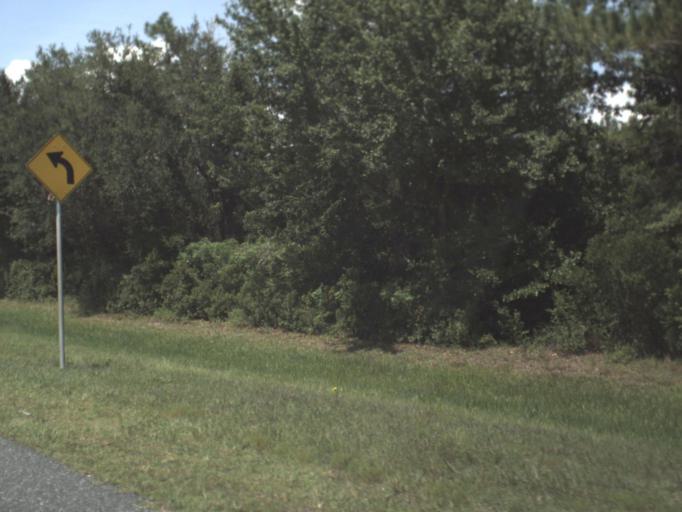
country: US
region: Florida
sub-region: Levy County
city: Inglis
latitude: 29.1573
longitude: -82.6386
